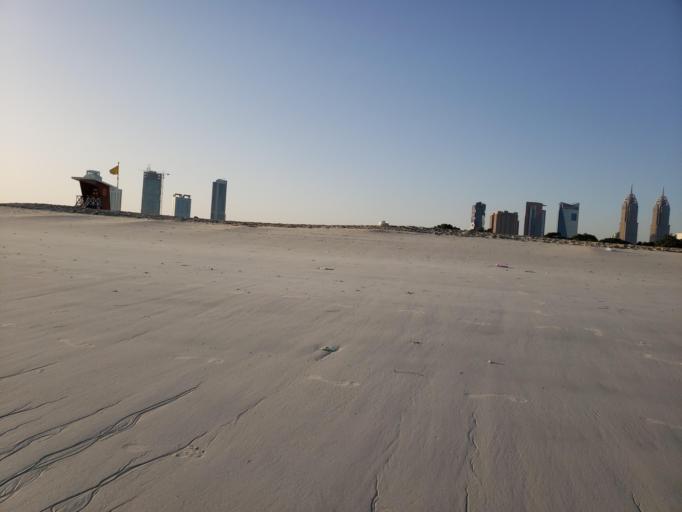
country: AE
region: Dubai
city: Dubai
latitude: 25.1161
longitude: 55.1651
